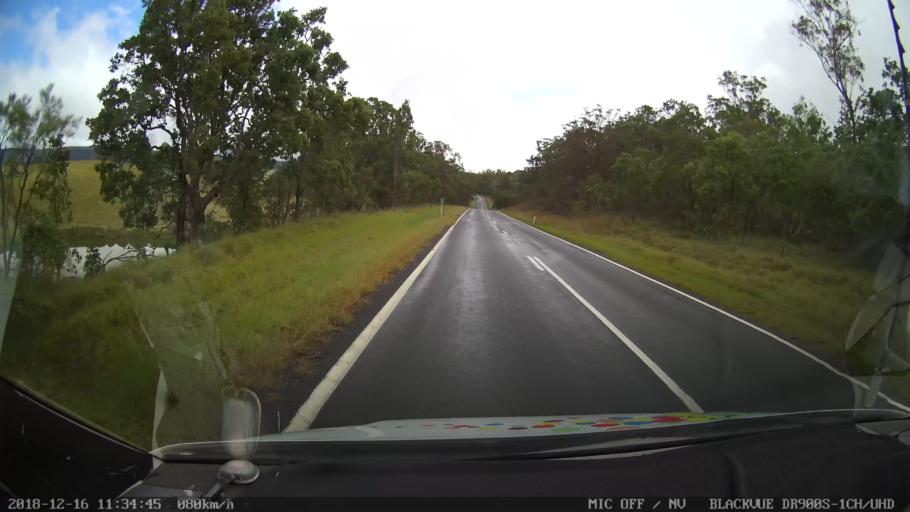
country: AU
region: New South Wales
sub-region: Tenterfield Municipality
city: Carrolls Creek
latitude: -28.9968
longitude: 152.1572
